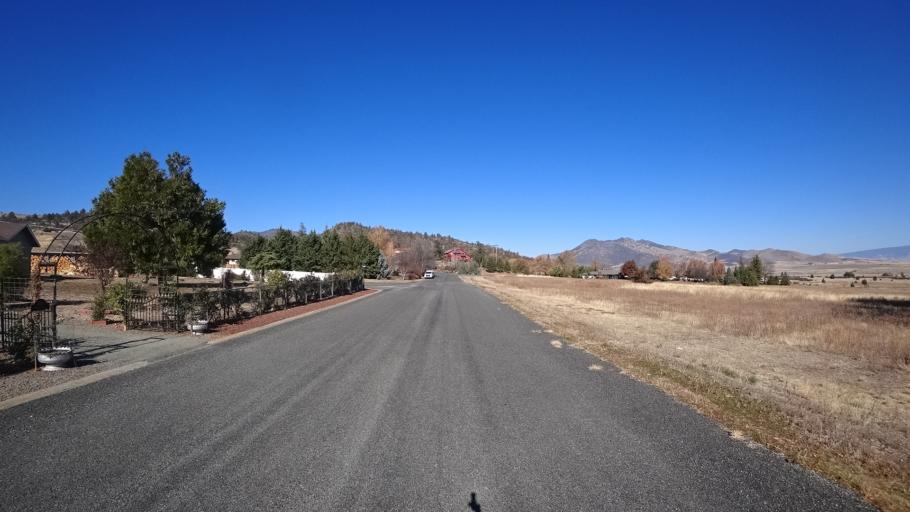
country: US
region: California
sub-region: Siskiyou County
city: Yreka
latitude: 41.7429
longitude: -122.6030
